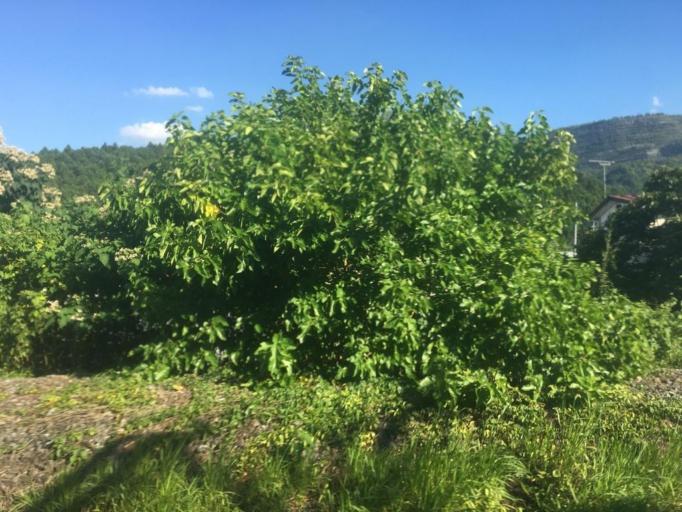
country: JP
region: Saitama
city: Chichibu
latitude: 35.9741
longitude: 139.0707
